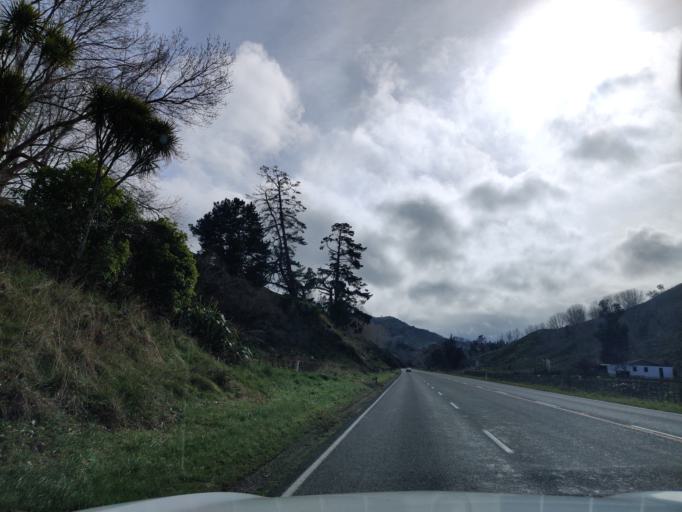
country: NZ
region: Manawatu-Wanganui
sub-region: Ruapehu District
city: Waiouru
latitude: -39.7883
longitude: 175.7853
